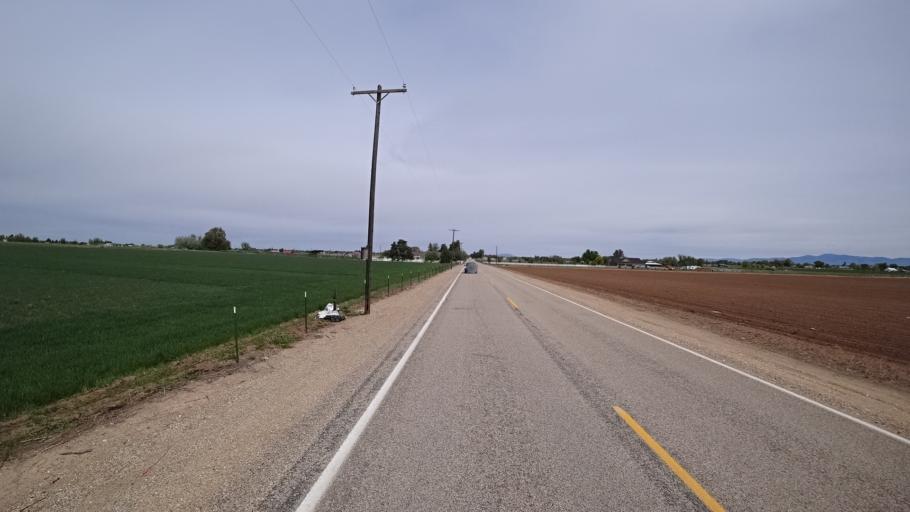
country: US
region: Idaho
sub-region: Ada County
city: Kuna
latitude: 43.5416
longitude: -116.4737
